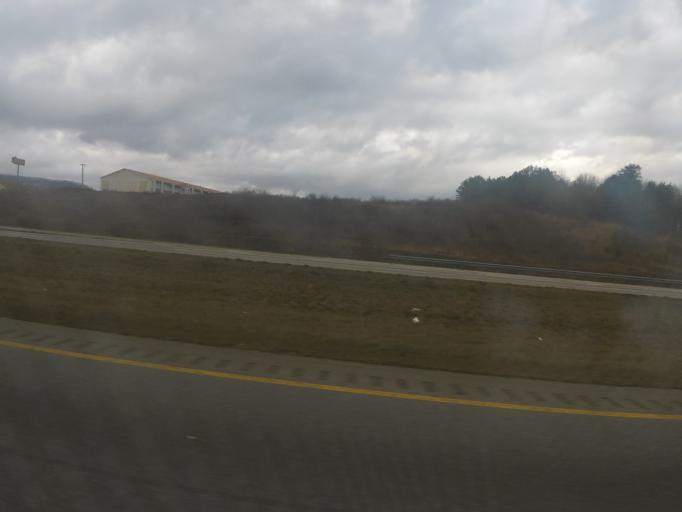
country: US
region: Tennessee
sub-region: Marion County
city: Jasper
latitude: 35.0486
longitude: -85.6274
